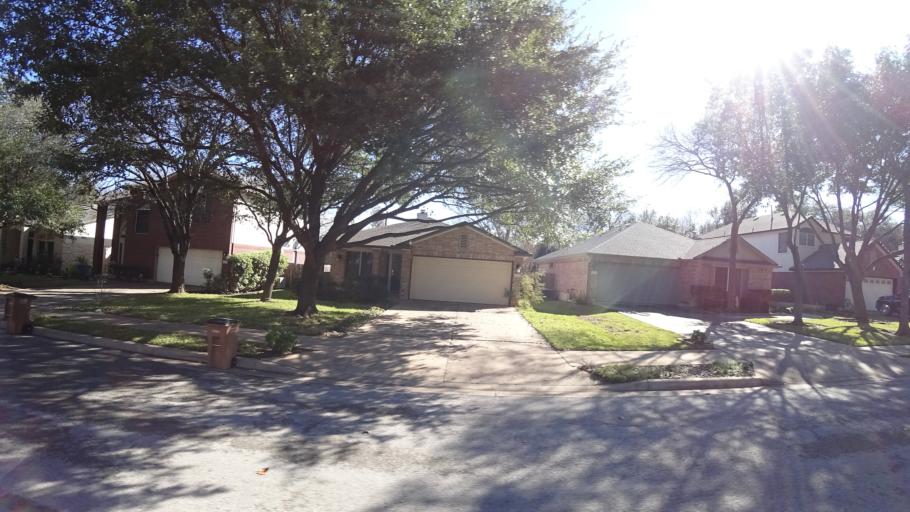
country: US
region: Texas
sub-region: Travis County
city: Wells Branch
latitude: 30.4282
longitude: -97.7157
